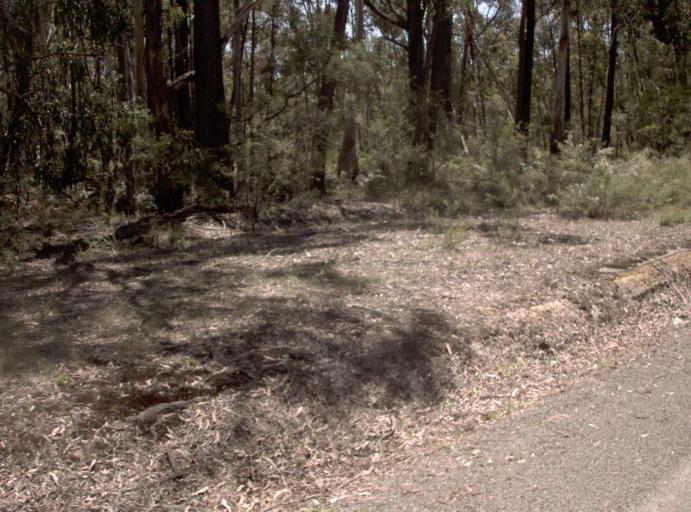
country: AU
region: Victoria
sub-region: East Gippsland
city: Lakes Entrance
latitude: -37.7650
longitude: 148.0585
